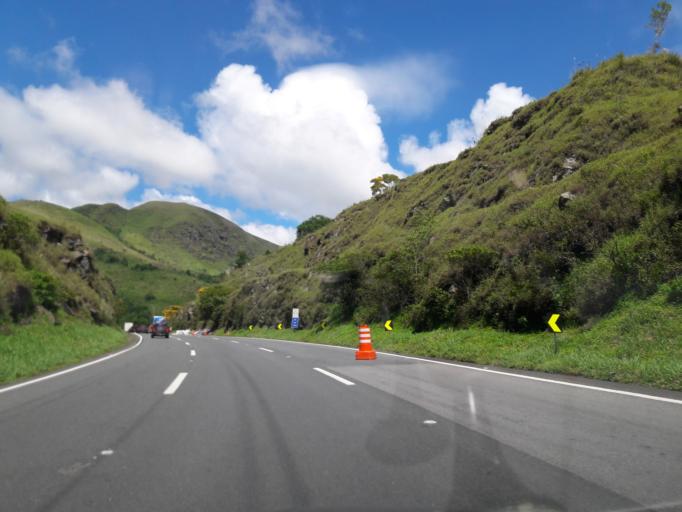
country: BR
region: Sao Paulo
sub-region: Cajati
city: Cajati
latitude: -24.9569
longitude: -48.4640
